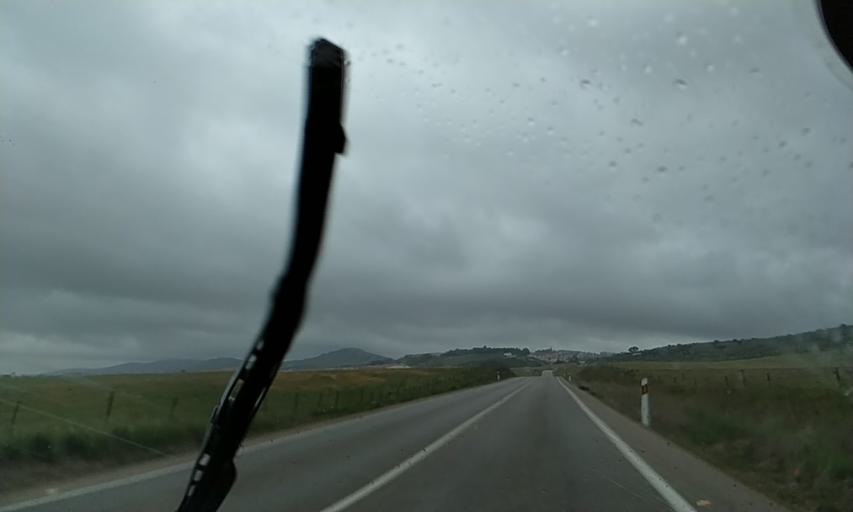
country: ES
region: Extremadura
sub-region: Provincia de Caceres
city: Caceres
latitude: 39.5002
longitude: -6.3884
